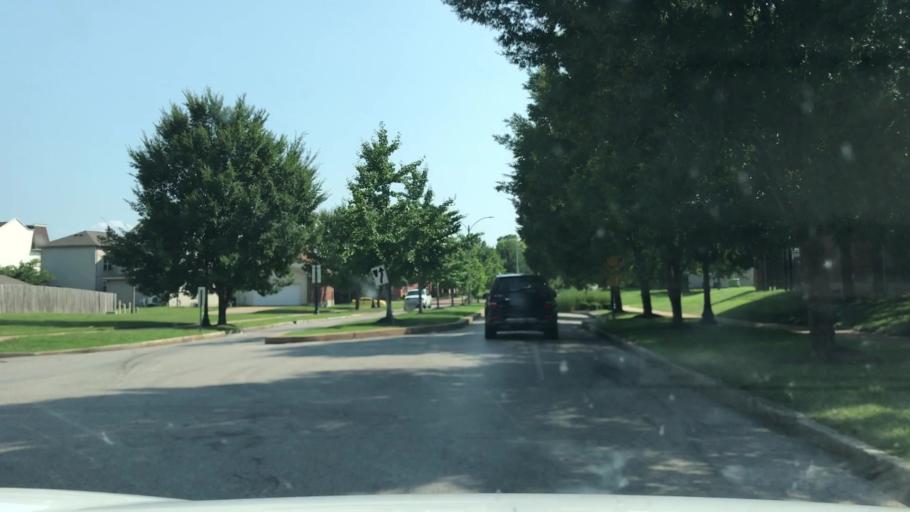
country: US
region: Missouri
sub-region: City of Saint Louis
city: St. Louis
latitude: 38.6163
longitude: -90.2057
